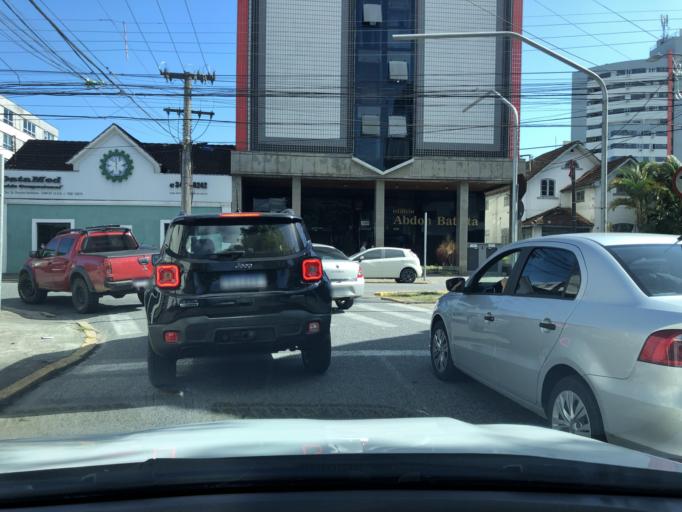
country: BR
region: Santa Catarina
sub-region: Joinville
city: Joinville
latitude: -26.3055
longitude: -48.8421
